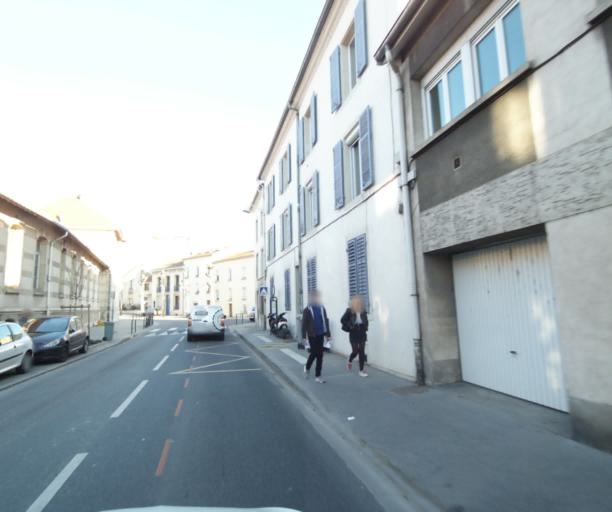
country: FR
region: Lorraine
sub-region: Departement de Meurthe-et-Moselle
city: Nancy
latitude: 48.6986
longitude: 6.1921
